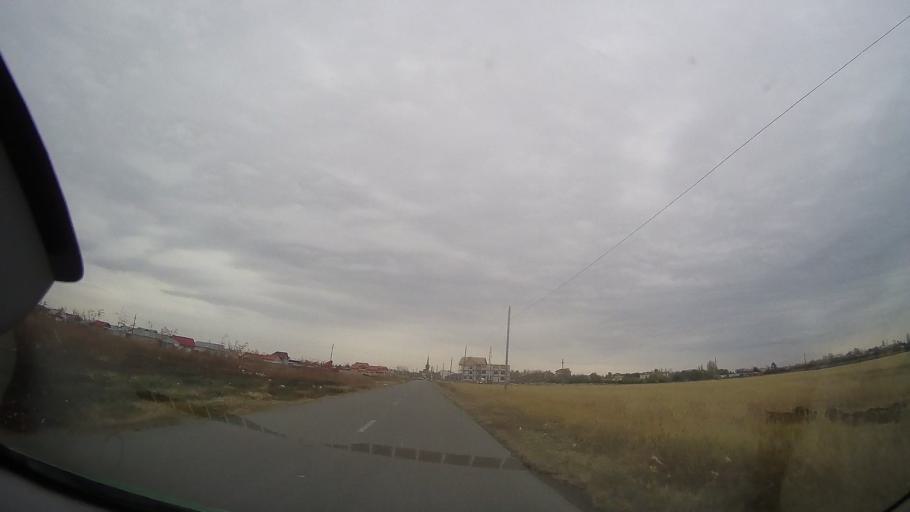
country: RO
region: Prahova
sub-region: Oras Mizil
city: Mizil
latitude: 45.0046
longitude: 26.4276
